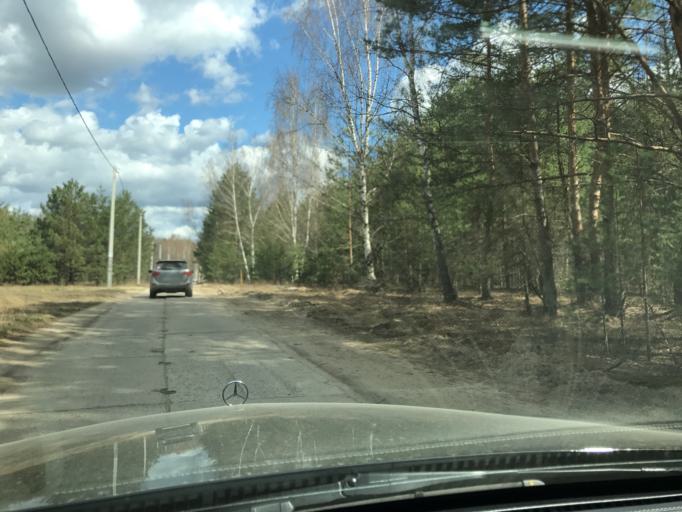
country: RU
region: Vladimir
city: Pokrov
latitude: 55.8587
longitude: 39.2035
